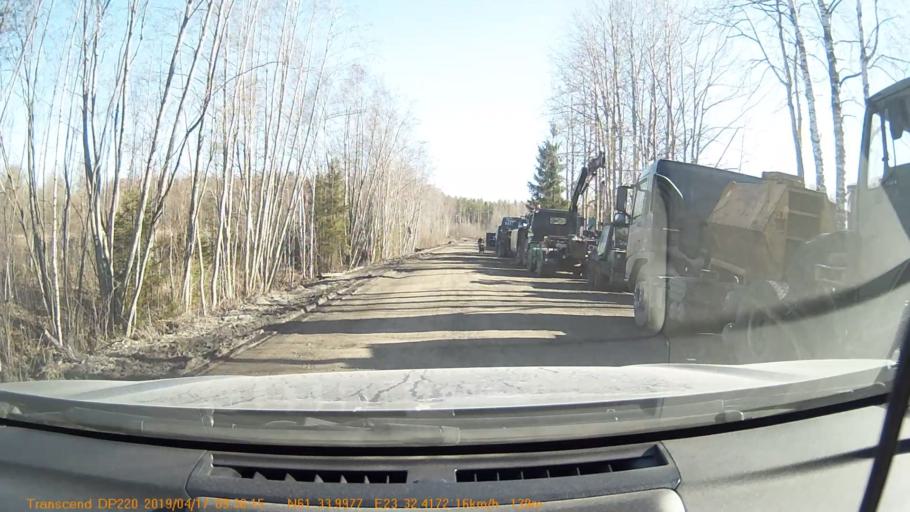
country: FI
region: Pirkanmaa
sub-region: Tampere
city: Yloejaervi
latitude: 61.5667
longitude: 23.5405
